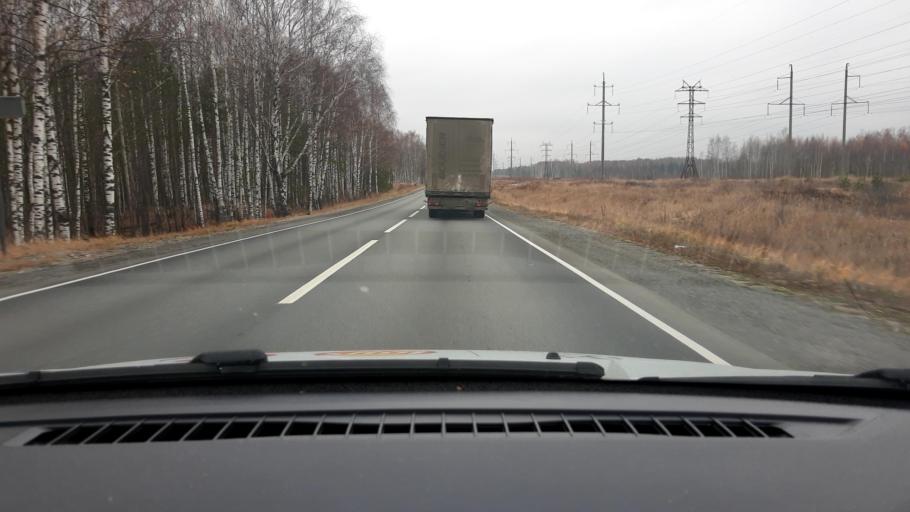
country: RU
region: Nizjnij Novgorod
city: Lukino
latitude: 56.3577
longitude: 43.5929
